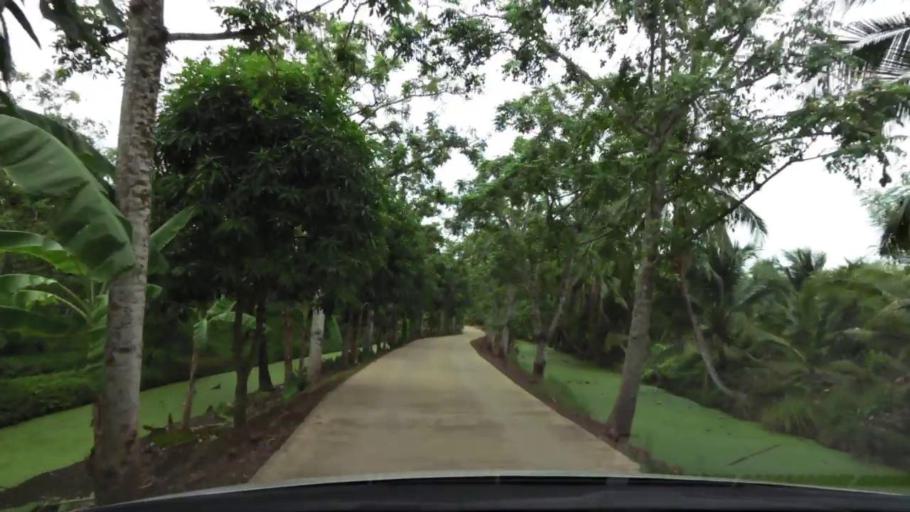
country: TH
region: Ratchaburi
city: Damnoen Saduak
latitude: 13.5564
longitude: 99.9968
